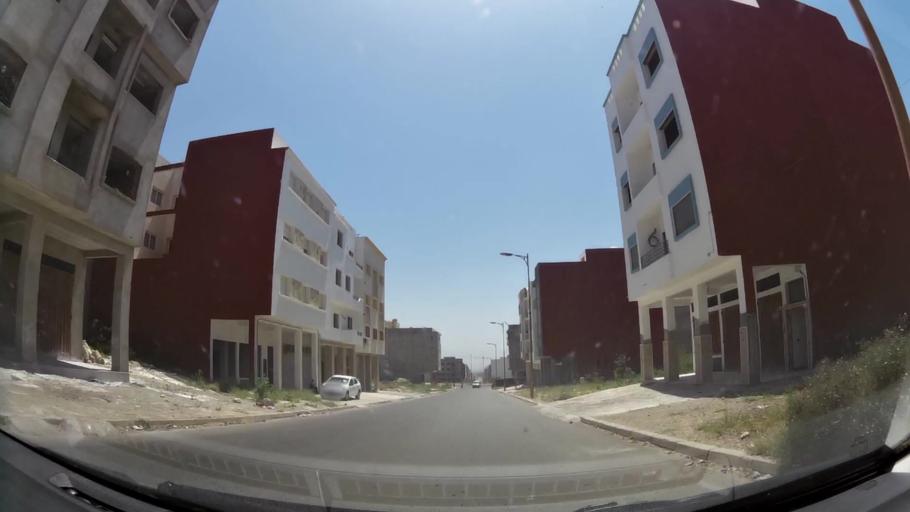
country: MA
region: Oued ed Dahab-Lagouira
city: Dakhla
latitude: 30.4409
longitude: -9.5563
